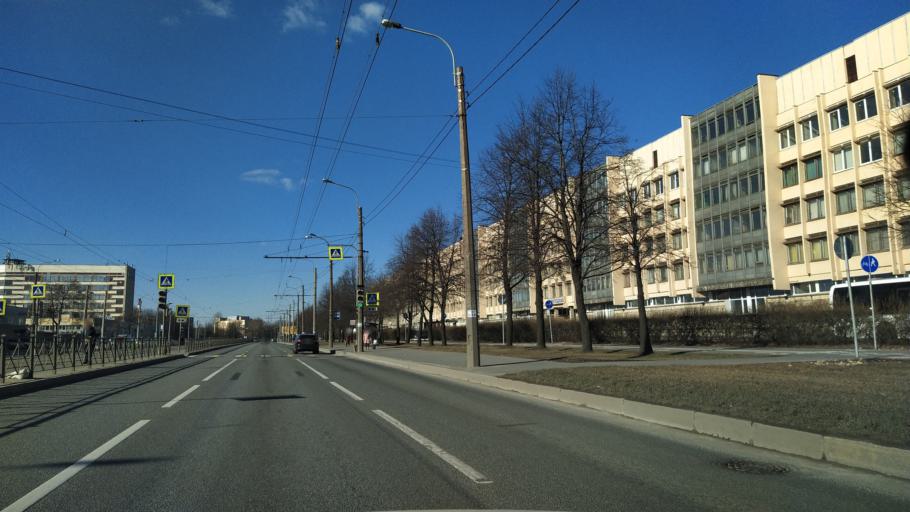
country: RU
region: St.-Petersburg
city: Kupchino
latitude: 59.8903
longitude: 30.3609
